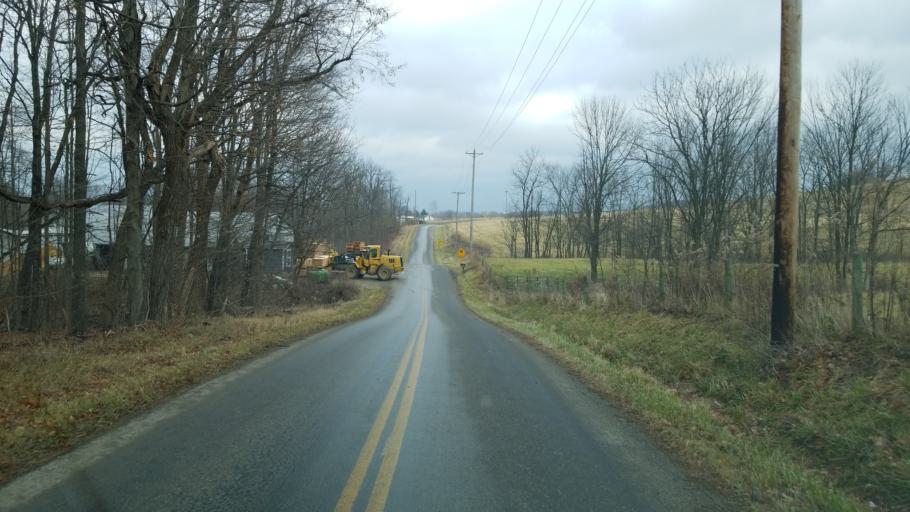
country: US
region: Ohio
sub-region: Holmes County
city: Millersburg
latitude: 40.5862
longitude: -81.9625
